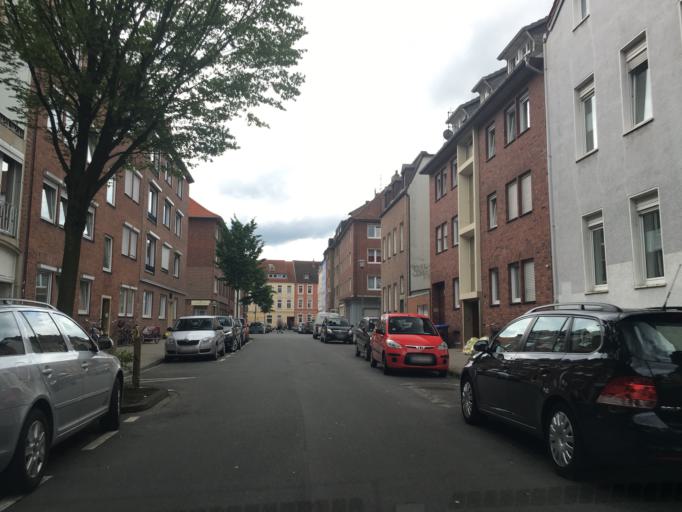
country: DE
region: North Rhine-Westphalia
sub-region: Regierungsbezirk Munster
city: Muenster
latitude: 51.9586
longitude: 7.6446
